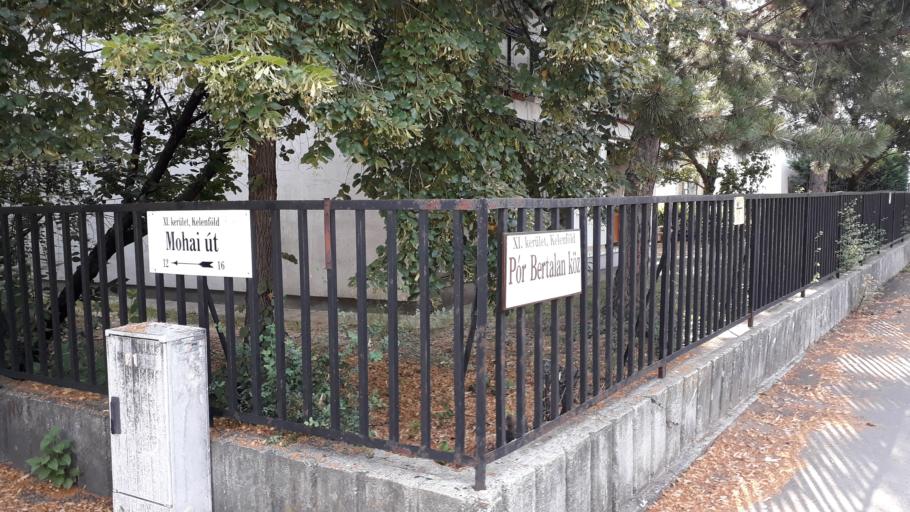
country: HU
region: Budapest
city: Budapest XI. keruelet
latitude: 47.4692
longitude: 19.0408
